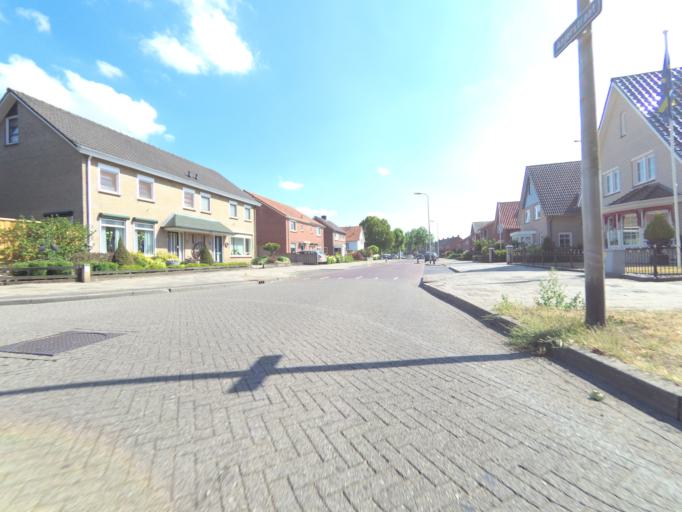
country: NL
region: Overijssel
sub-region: Gemeente Oldenzaal
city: Oldenzaal
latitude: 52.3166
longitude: 6.9223
